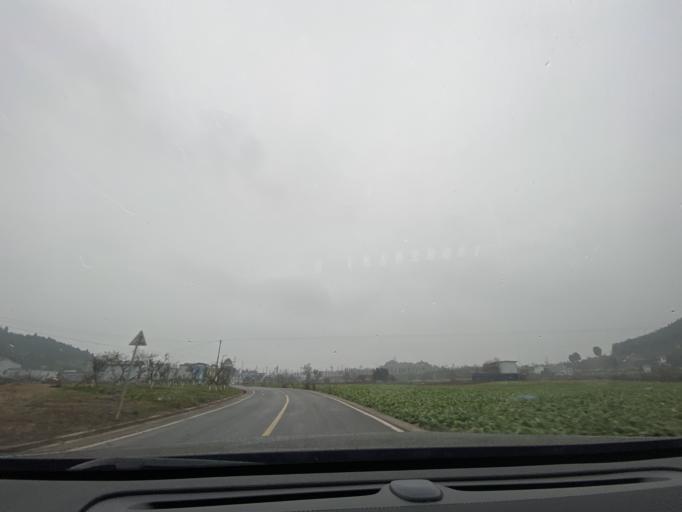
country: CN
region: Sichuan
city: Jiancheng
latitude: 30.3918
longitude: 104.6359
